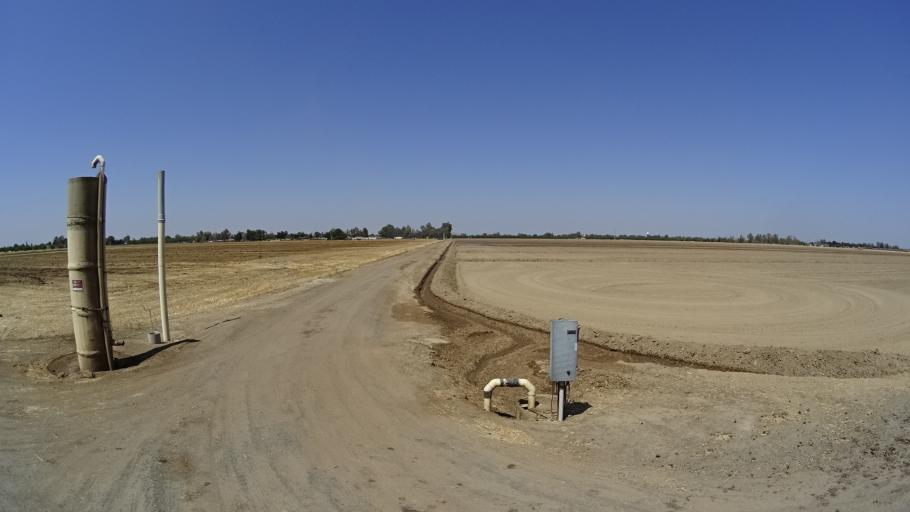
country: US
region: California
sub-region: Kings County
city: Home Garden
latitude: 36.3058
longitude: -119.6101
